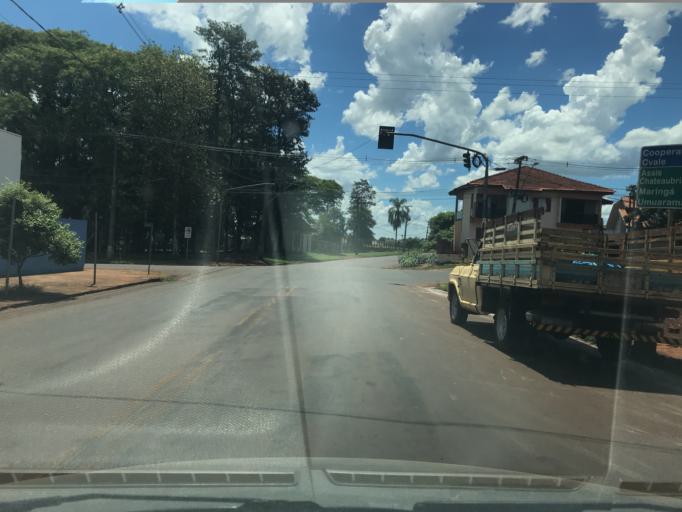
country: BR
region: Parana
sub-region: Palotina
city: Palotina
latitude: -24.2802
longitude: -53.8484
